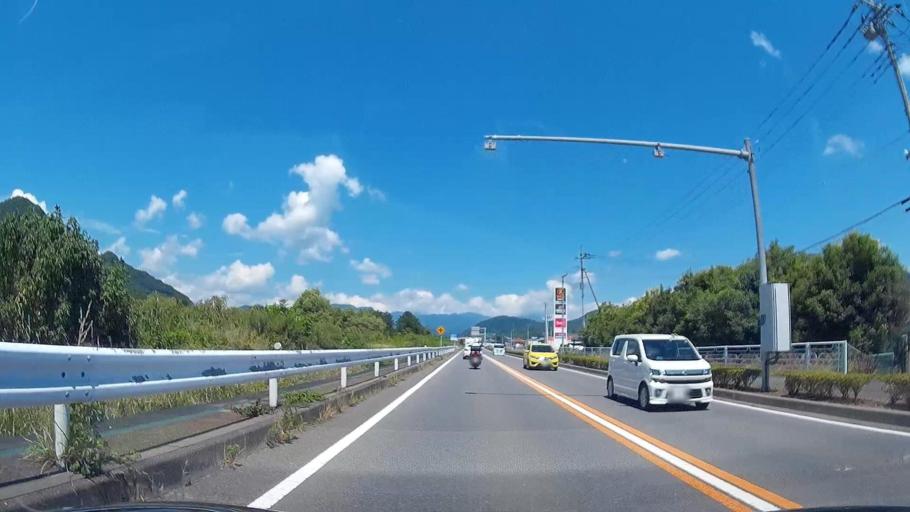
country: JP
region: Gunma
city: Numata
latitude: 36.6565
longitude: 139.0203
